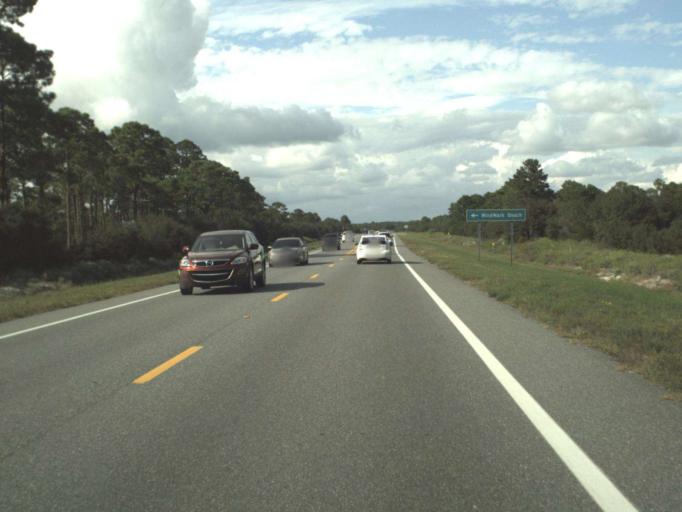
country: US
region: Florida
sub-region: Gulf County
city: Port Saint Joe
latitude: 29.8585
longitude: -85.3361
